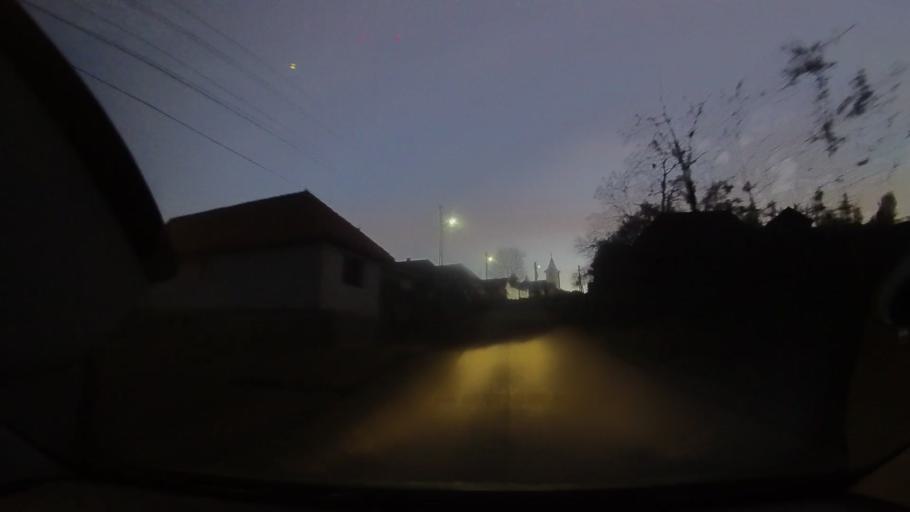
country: RO
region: Bihor
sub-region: Comuna Varciorog
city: Varciorog
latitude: 46.9765
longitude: 22.3254
